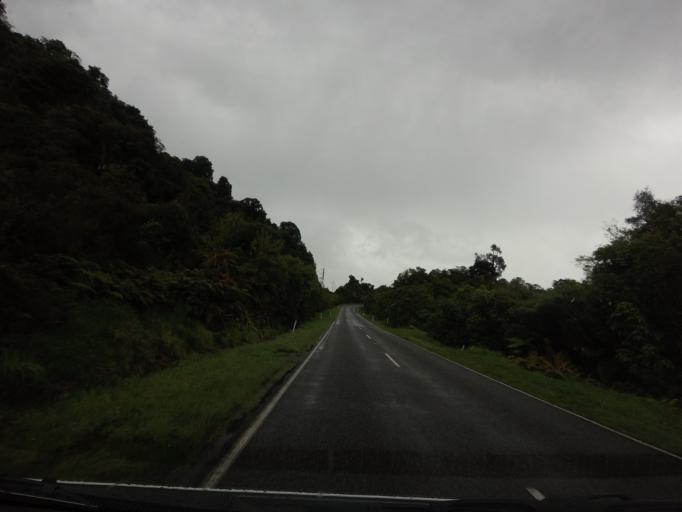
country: NZ
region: West Coast
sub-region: Westland District
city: Hokitika
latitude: -43.0653
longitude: 170.6309
